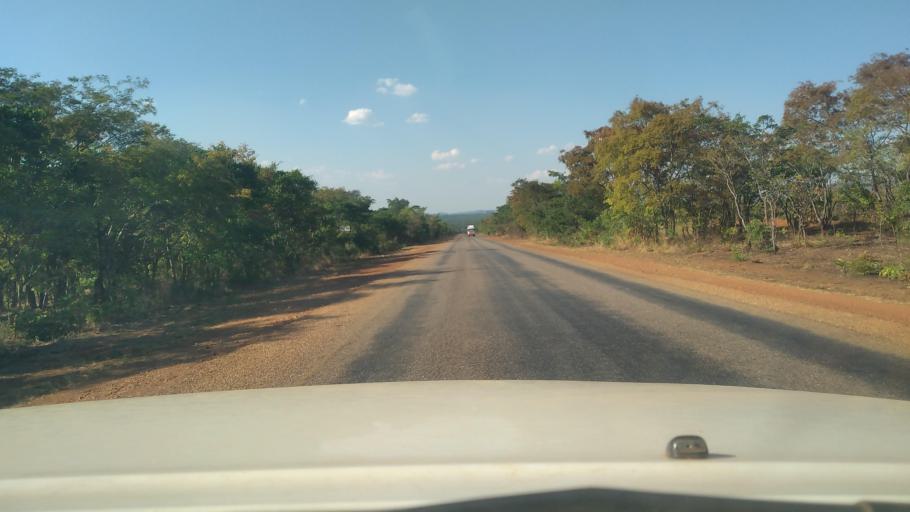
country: ZM
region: Northern
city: Mpika
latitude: -11.7578
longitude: 31.4635
